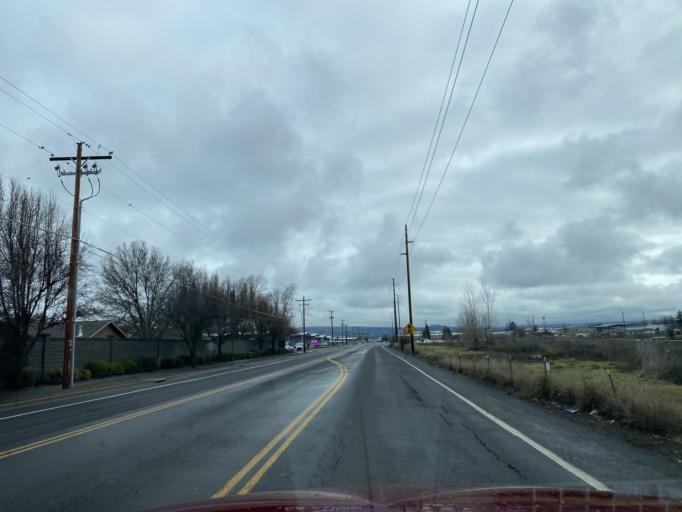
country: US
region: Oregon
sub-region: Jackson County
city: Medford
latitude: 42.3408
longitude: -122.9035
